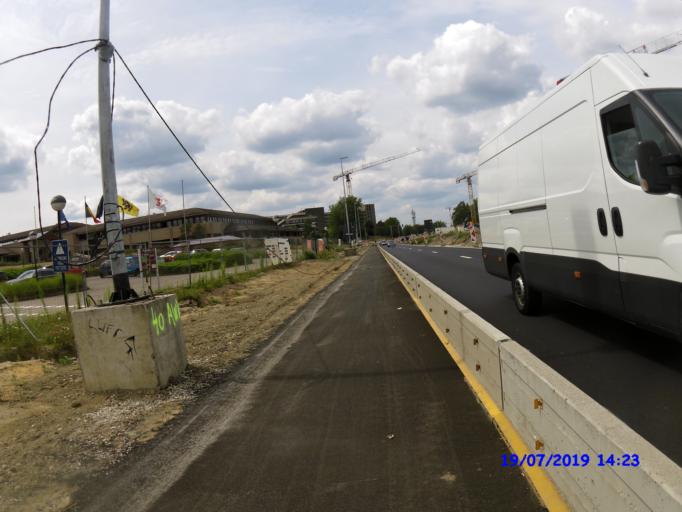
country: BE
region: Flanders
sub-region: Provincie Limburg
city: Hasselt
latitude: 50.9310
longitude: 5.3638
